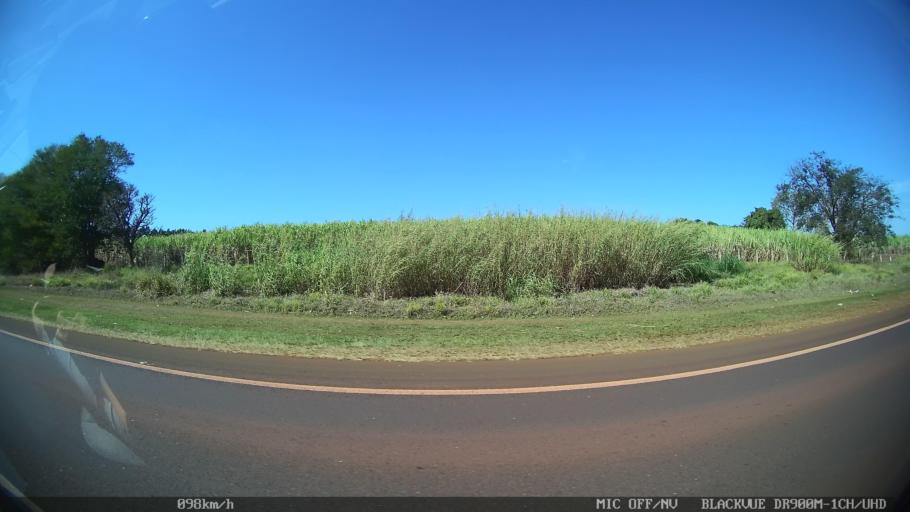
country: BR
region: Sao Paulo
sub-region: Franca
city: Franca
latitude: -20.6497
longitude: -47.4845
